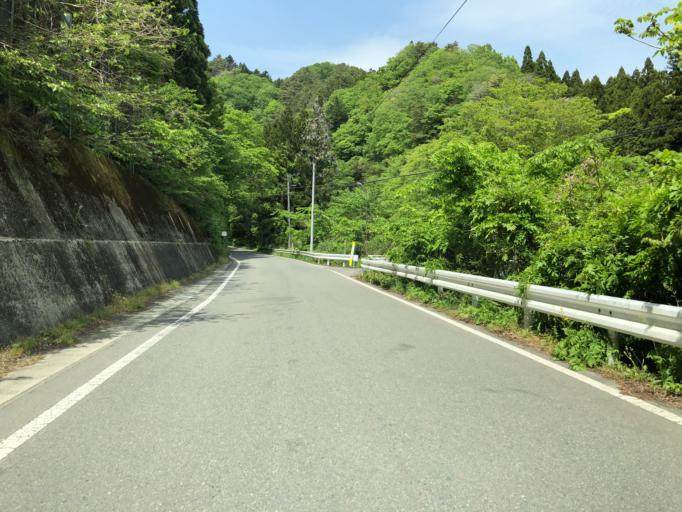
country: JP
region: Fukushima
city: Namie
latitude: 37.6899
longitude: 140.9155
